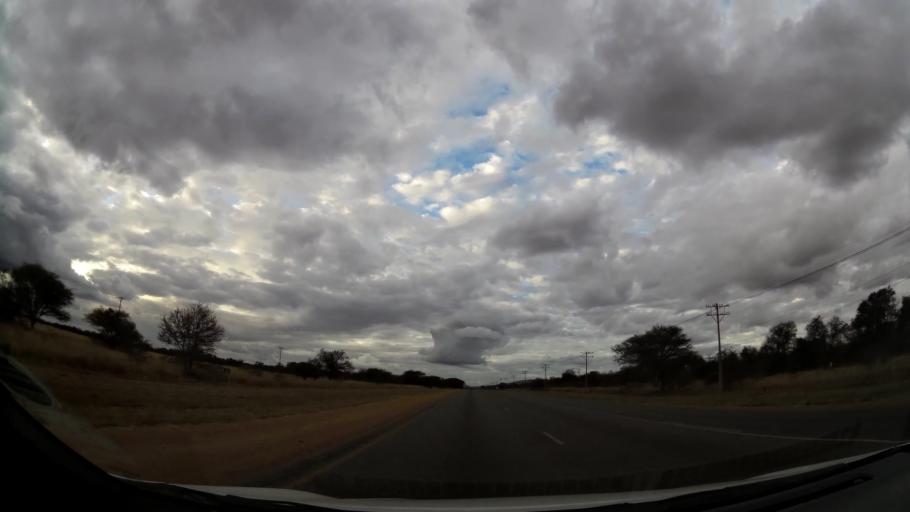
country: ZA
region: Limpopo
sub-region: Waterberg District Municipality
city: Mokopane
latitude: -24.2379
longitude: 28.9960
